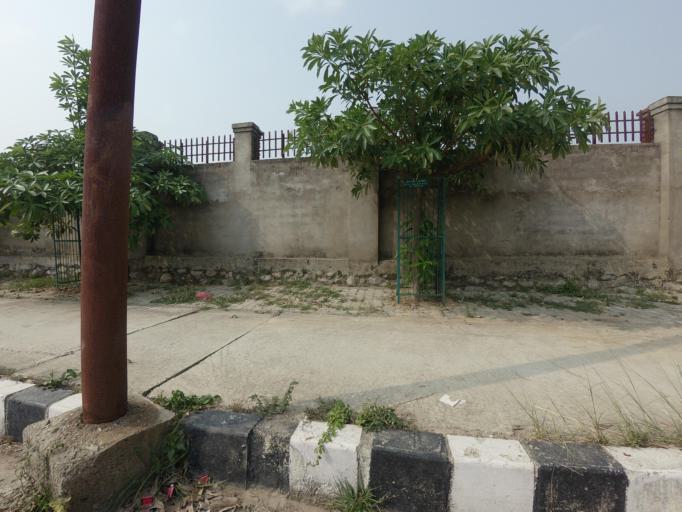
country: NP
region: Western Region
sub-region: Lumbini Zone
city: Bhairahawa
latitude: 27.5269
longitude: 83.4579
